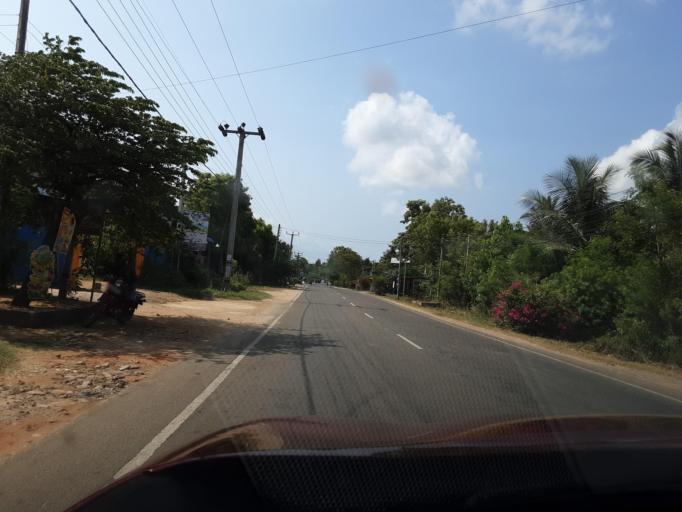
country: LK
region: Southern
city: Tangalla
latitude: 6.3007
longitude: 81.2358
